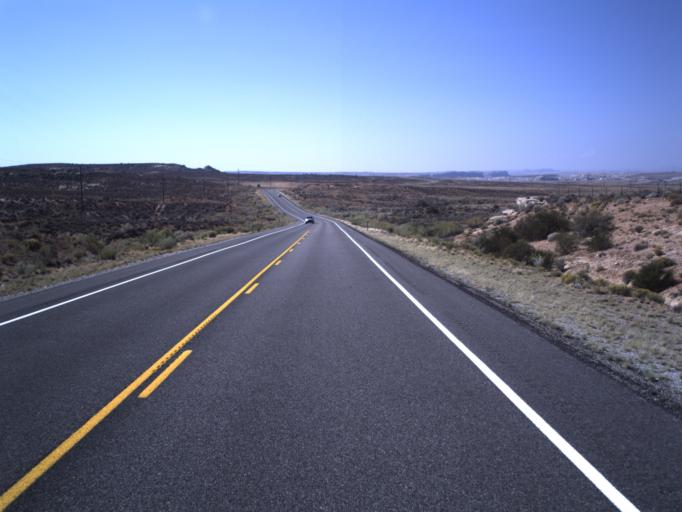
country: US
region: Utah
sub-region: San Juan County
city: Blanding
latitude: 37.3762
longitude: -109.5046
